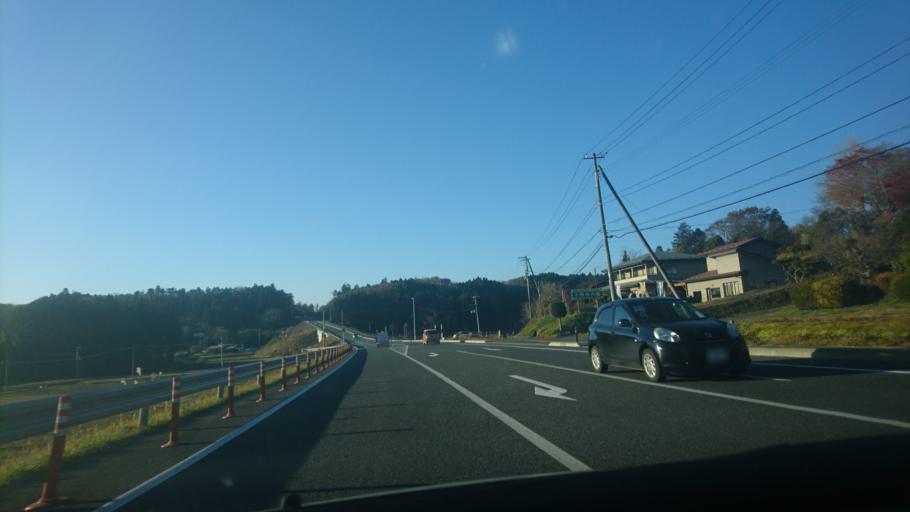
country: JP
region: Iwate
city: Ichinoseki
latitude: 38.9019
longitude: 141.1811
